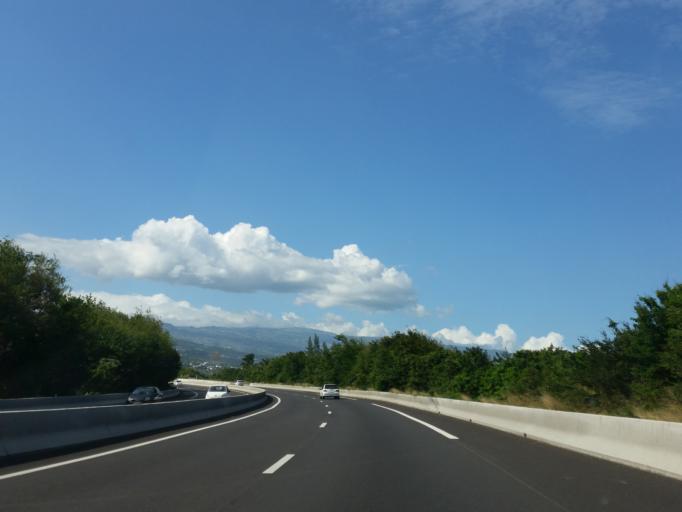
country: RE
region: Reunion
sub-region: Reunion
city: Saint-Louis
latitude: -21.2841
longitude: 55.3736
